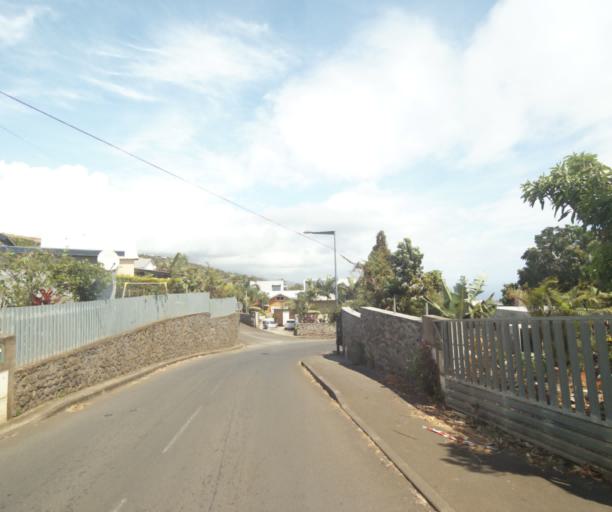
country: RE
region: Reunion
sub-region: Reunion
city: Trois-Bassins
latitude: -21.0987
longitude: 55.2738
